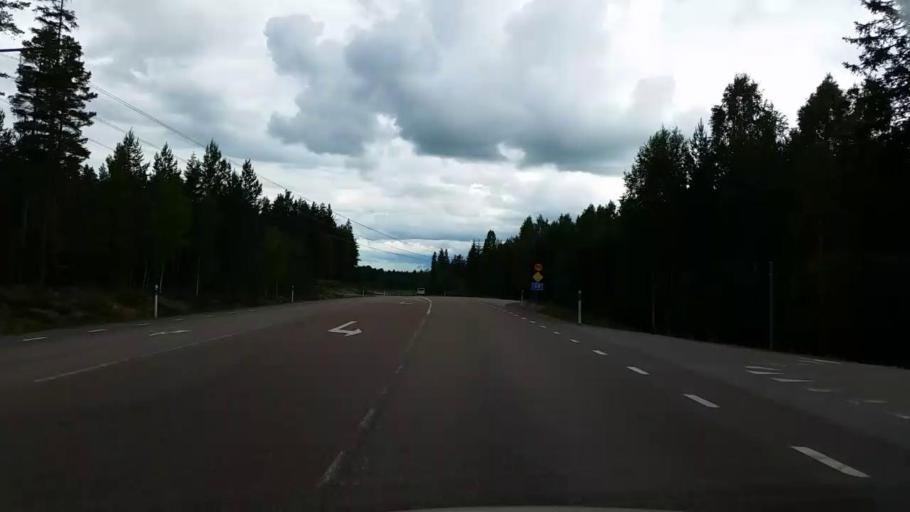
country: SE
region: Dalarna
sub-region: Avesta Kommun
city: Horndal
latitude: 60.4709
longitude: 16.4486
